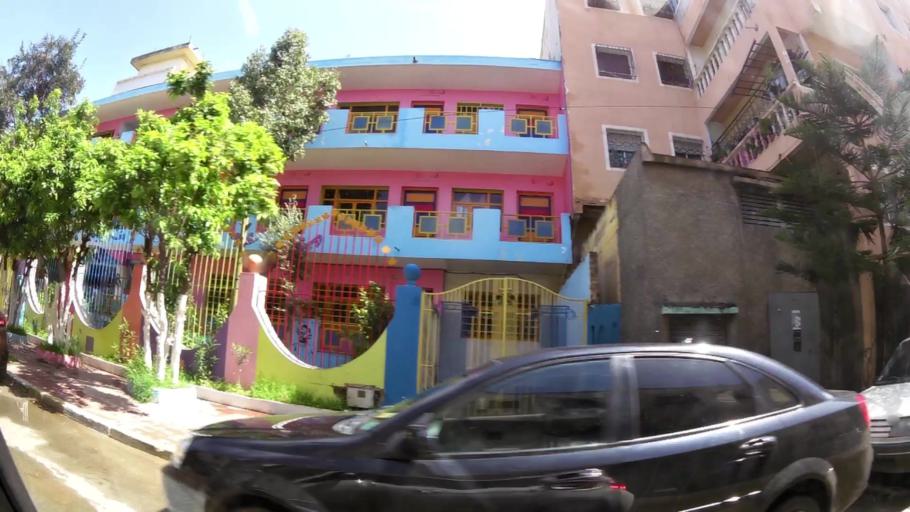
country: MA
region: Grand Casablanca
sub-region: Mohammedia
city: Mohammedia
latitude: 33.6378
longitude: -7.4479
